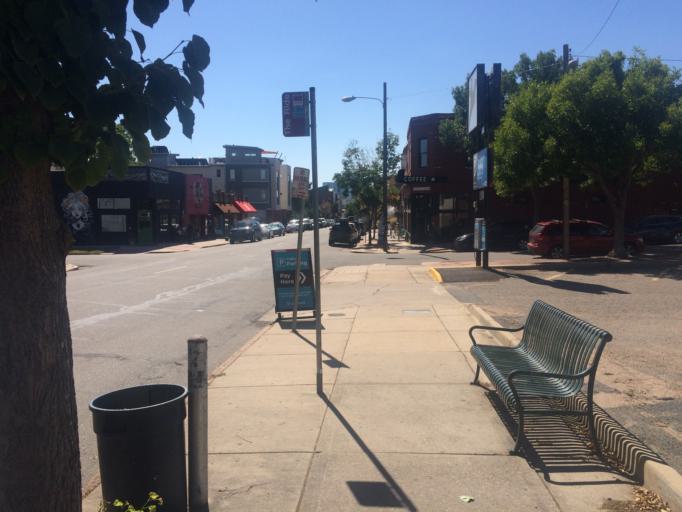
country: US
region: Colorado
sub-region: Denver County
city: Denver
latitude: 39.7684
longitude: -105.0043
